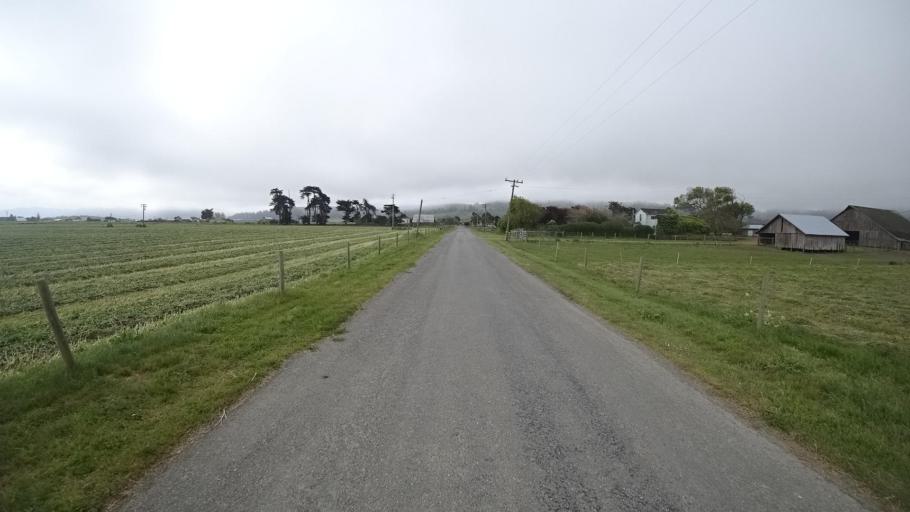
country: US
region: California
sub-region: Humboldt County
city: Fortuna
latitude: 40.5688
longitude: -124.1878
